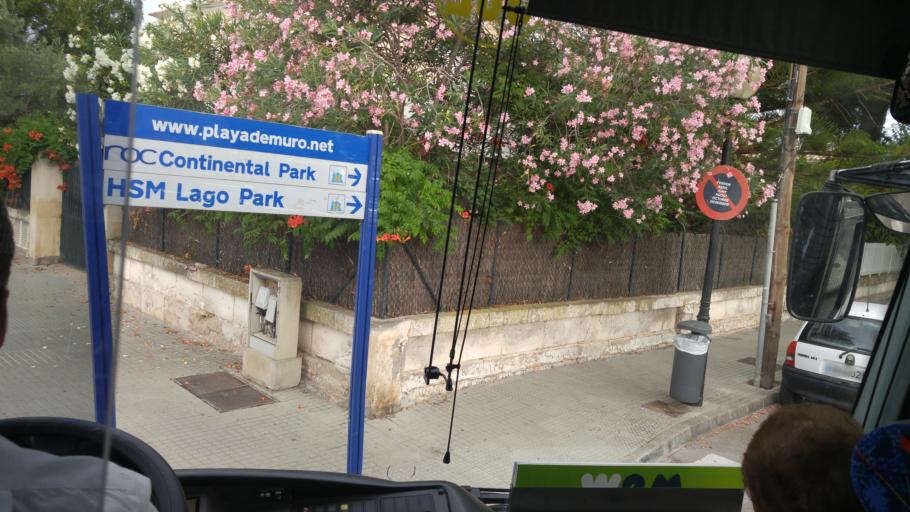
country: ES
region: Balearic Islands
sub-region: Illes Balears
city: Port d'Alcudia
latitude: 39.8131
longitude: 3.1136
